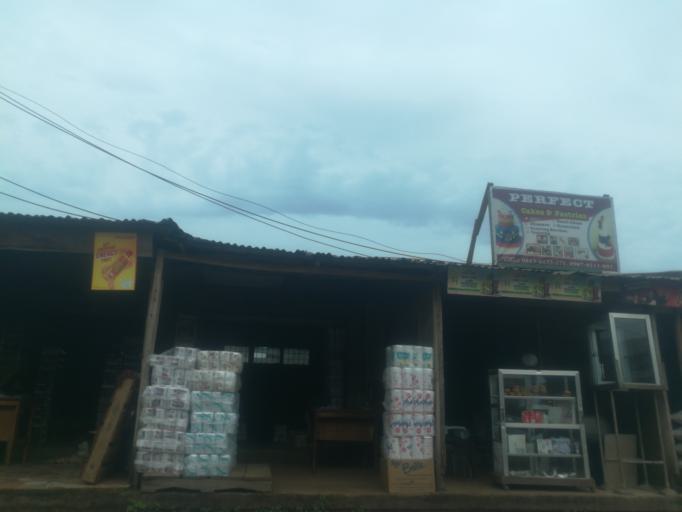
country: NG
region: Oyo
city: Ibadan
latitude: 7.3907
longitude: 3.9533
